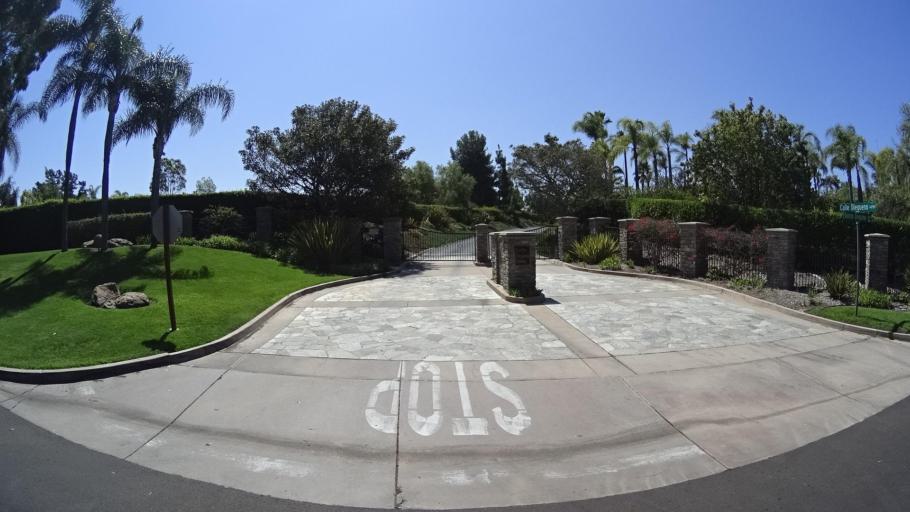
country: US
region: California
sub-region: San Diego County
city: Fairbanks Ranch
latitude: 32.9827
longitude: -117.1886
